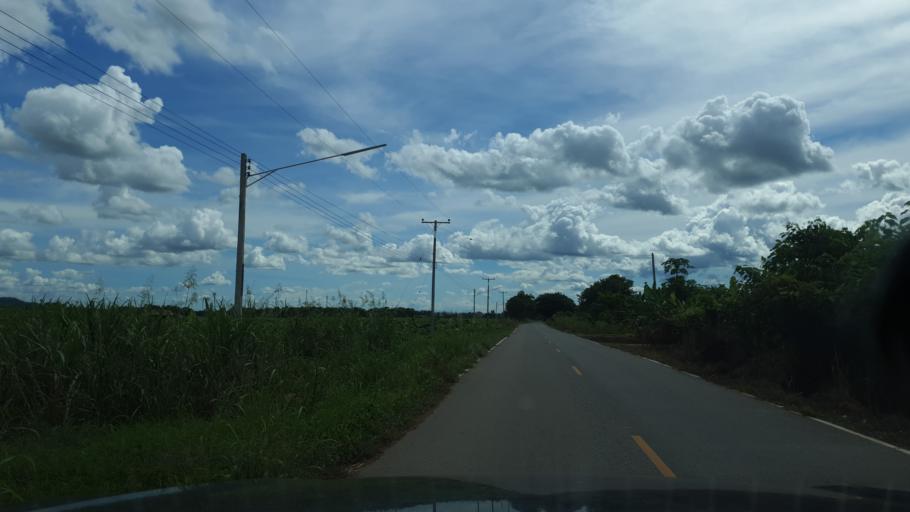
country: TH
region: Sukhothai
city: Thung Saliam
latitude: 17.3434
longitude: 99.6381
